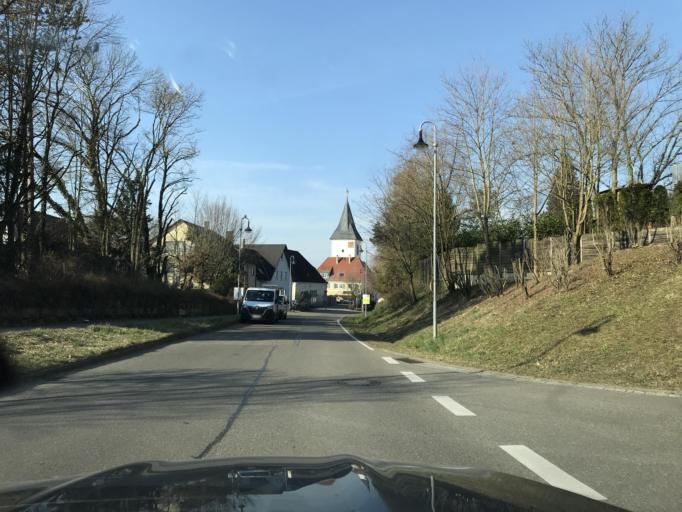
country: DE
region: Baden-Wuerttemberg
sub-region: Regierungsbezirk Stuttgart
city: Schwaikheim
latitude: 48.8783
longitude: 9.3522
